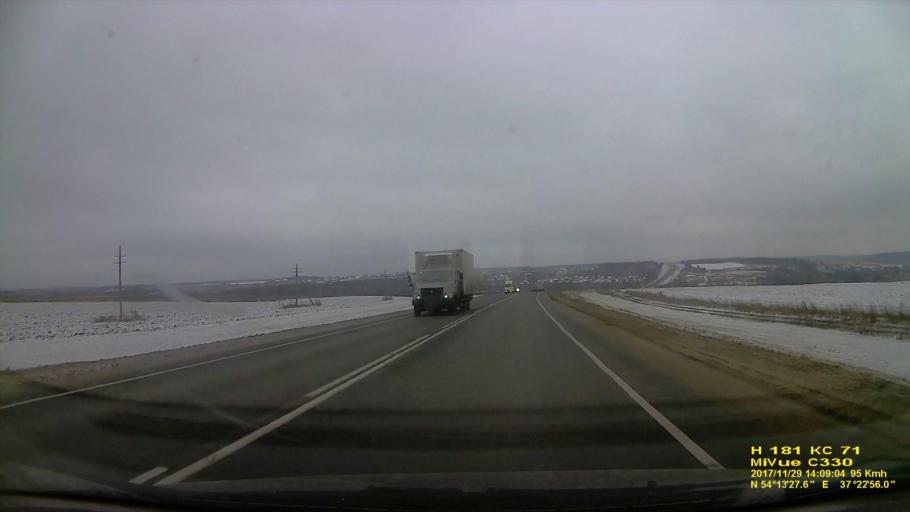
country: RU
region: Tula
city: Leninskiy
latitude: 54.2241
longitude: 37.3827
